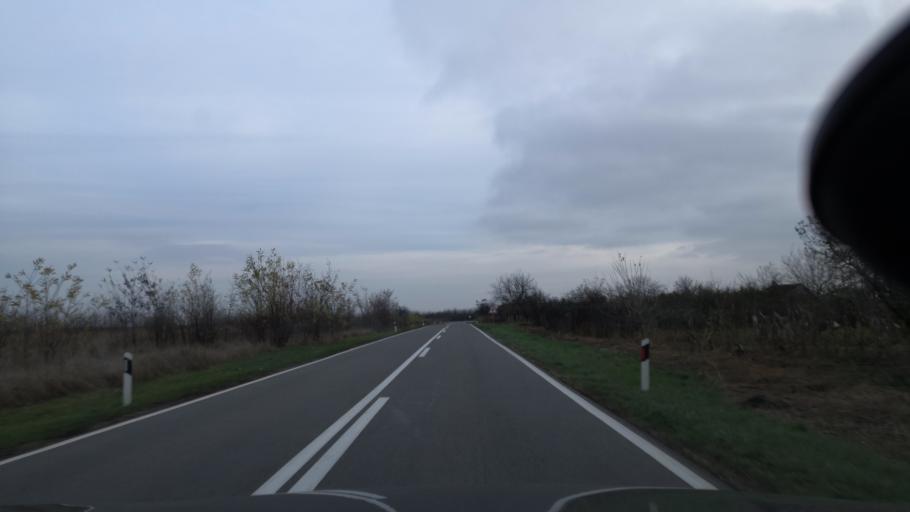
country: RS
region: Autonomna Pokrajina Vojvodina
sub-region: Severnobanatski Okrug
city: Coka
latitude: 45.9636
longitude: 20.1306
